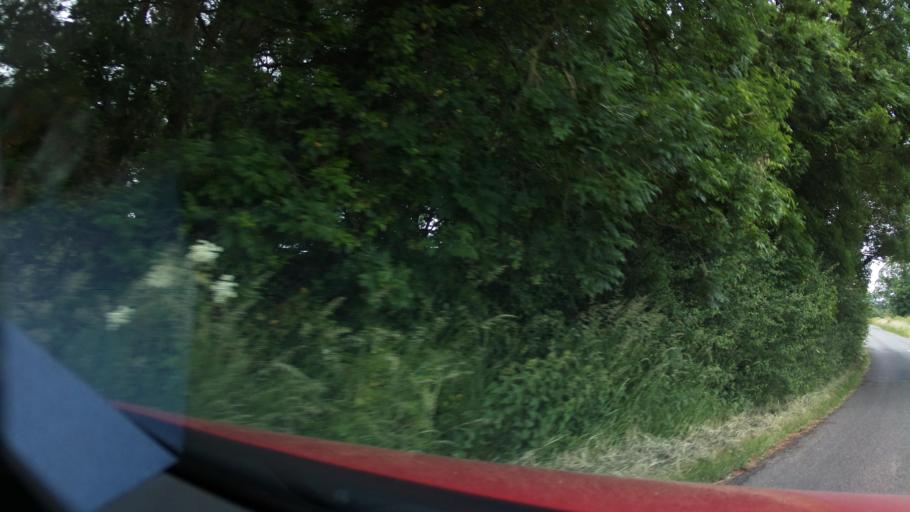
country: GB
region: England
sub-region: Leicestershire
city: Melton Mowbray
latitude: 52.7154
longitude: -0.8299
